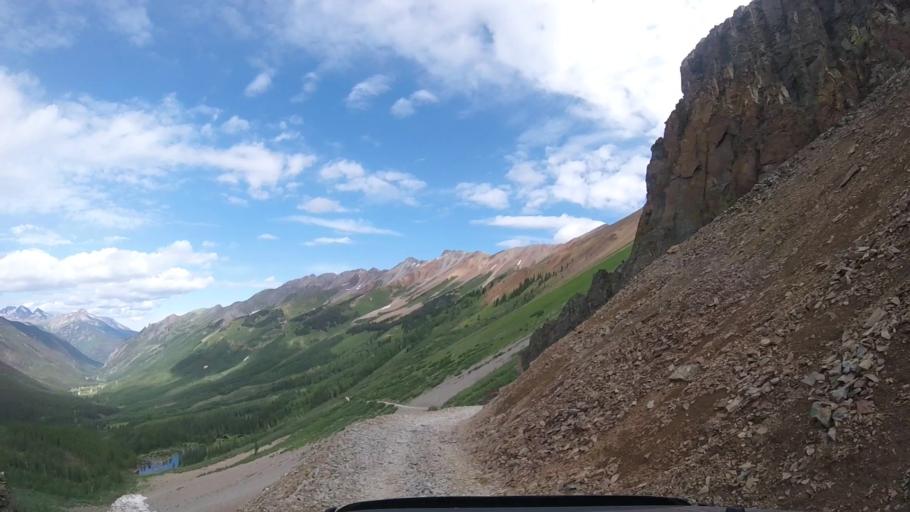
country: US
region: Colorado
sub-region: San Miguel County
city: Telluride
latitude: 37.8549
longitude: -107.7866
